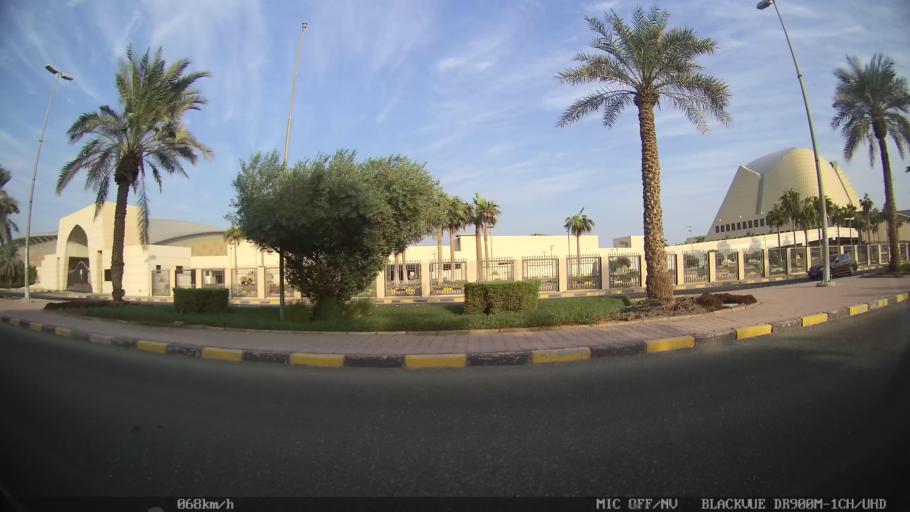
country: KW
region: Al Farwaniyah
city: Janub as Surrah
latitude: 29.2471
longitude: 47.9740
